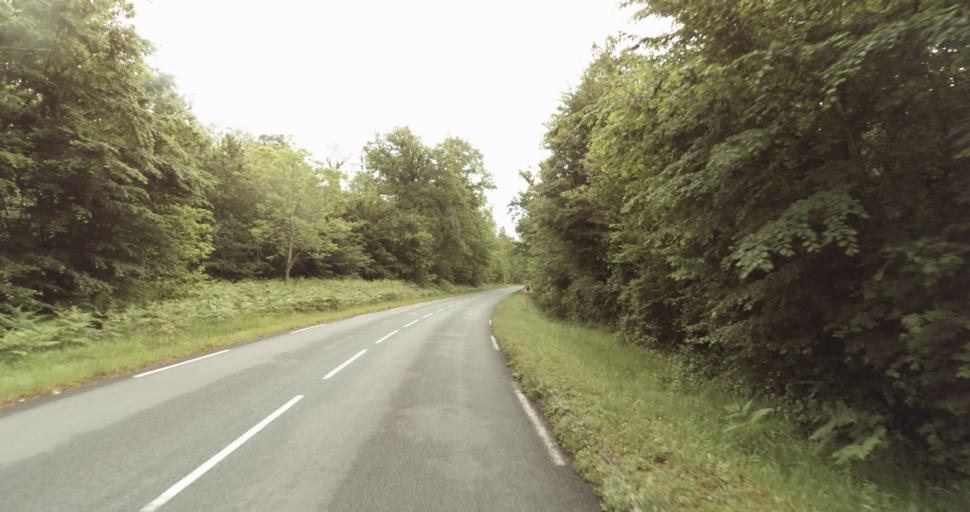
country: FR
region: Aquitaine
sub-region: Departement de la Dordogne
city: Belves
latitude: 44.6700
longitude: 1.0021
